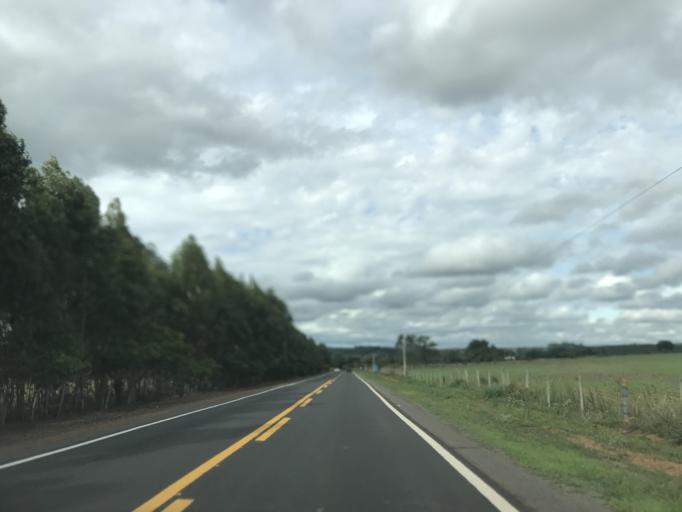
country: BR
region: Goias
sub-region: Bela Vista De Goias
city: Bela Vista de Goias
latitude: -17.1785
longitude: -48.6862
